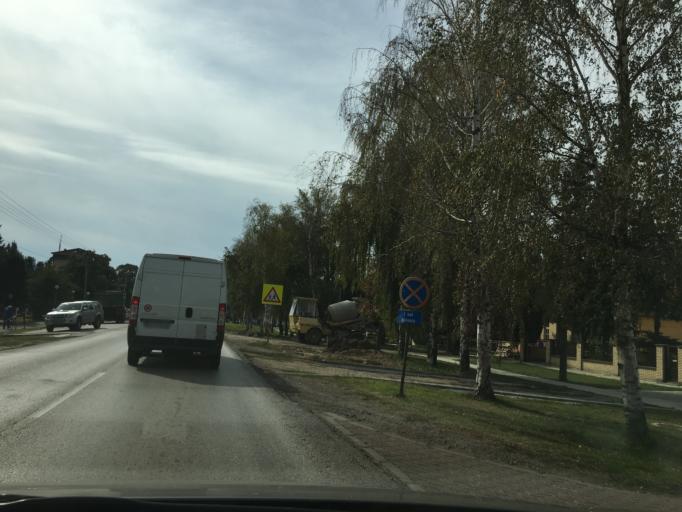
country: RS
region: Autonomna Pokrajina Vojvodina
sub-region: Juznobacki Okrug
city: Temerin
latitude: 45.3923
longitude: 19.8812
